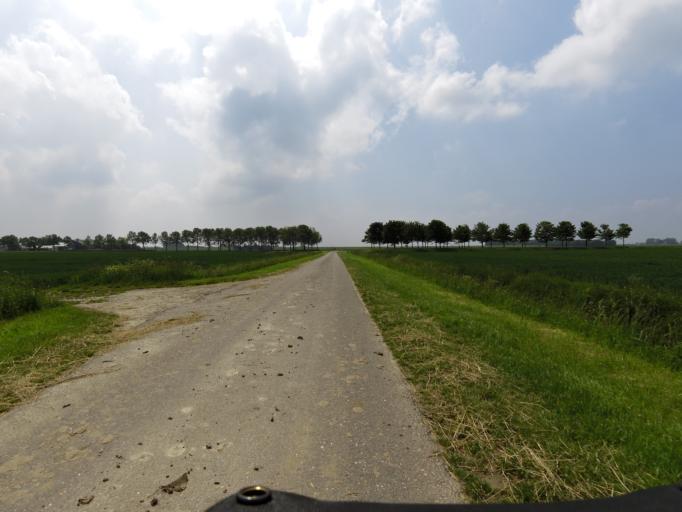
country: NL
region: South Holland
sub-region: Gemeente Spijkenisse
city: Spijkenisse
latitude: 51.8117
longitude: 4.2784
